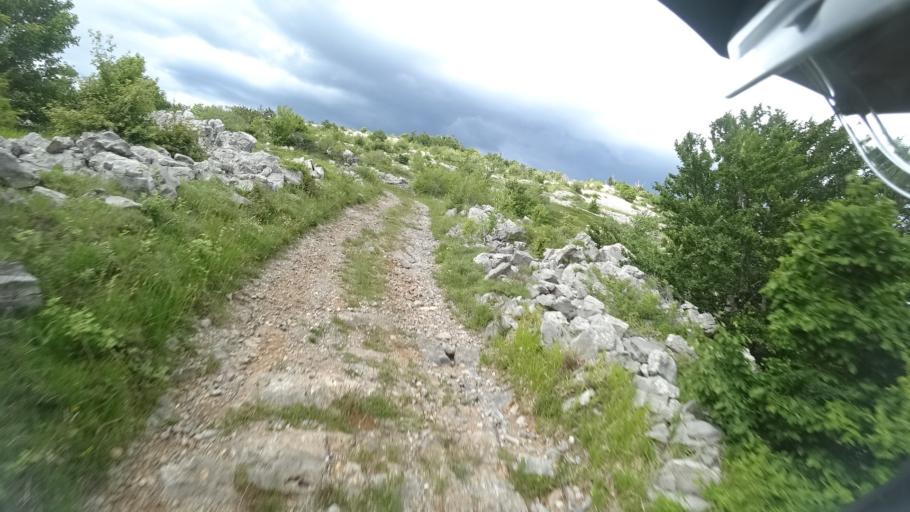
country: HR
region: Zadarska
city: Obrovac
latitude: 44.2683
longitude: 15.7393
